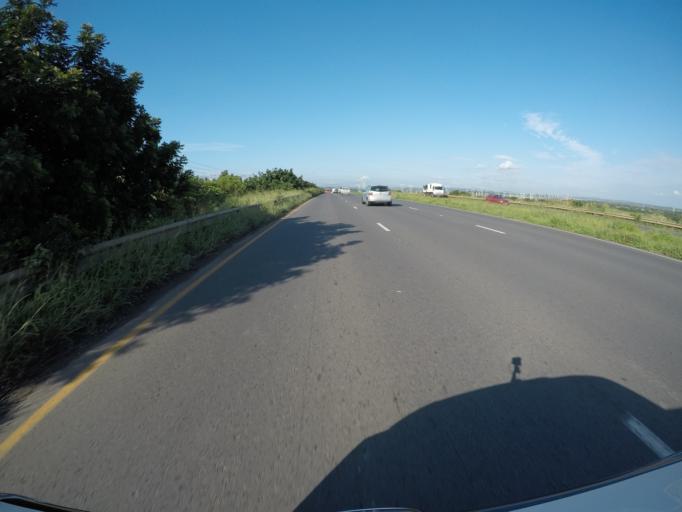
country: ZA
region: KwaZulu-Natal
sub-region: uThungulu District Municipality
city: Richards Bay
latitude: -28.7758
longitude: 32.0074
